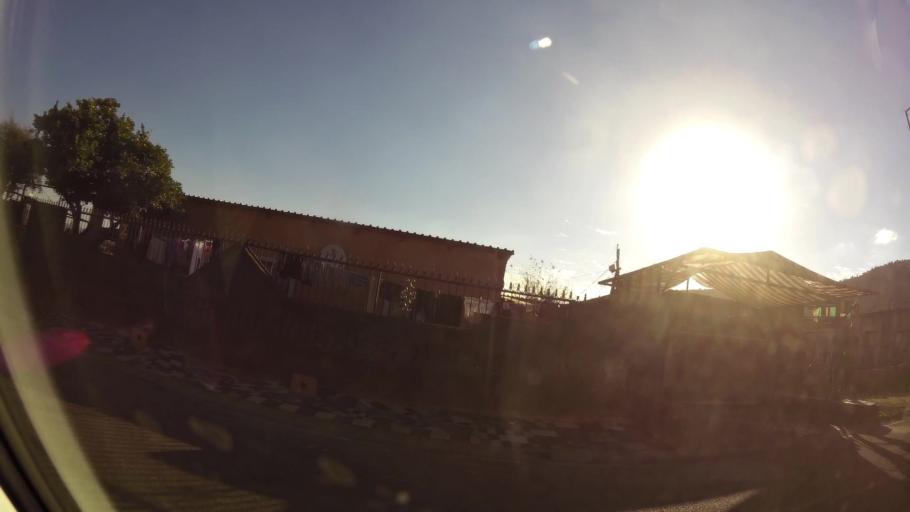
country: ZA
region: Gauteng
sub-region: City of Tshwane Metropolitan Municipality
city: Cullinan
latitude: -25.7038
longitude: 28.3733
